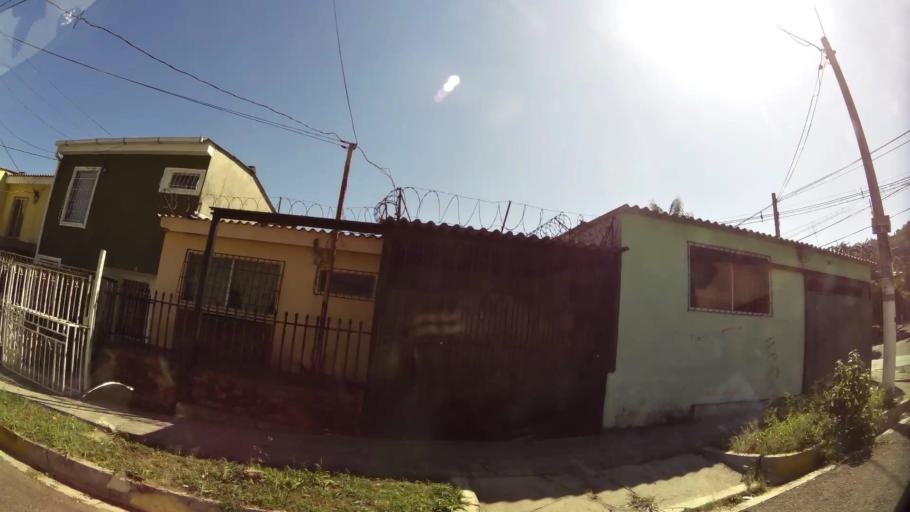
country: SV
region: La Libertad
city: Santa Tecla
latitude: 13.6670
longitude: -89.2895
